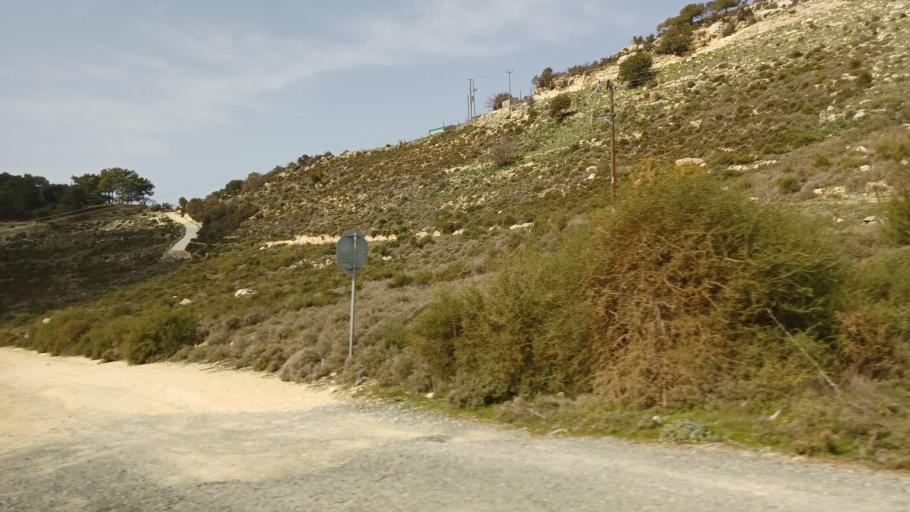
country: CY
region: Limassol
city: Pachna
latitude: 34.7672
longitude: 32.7038
